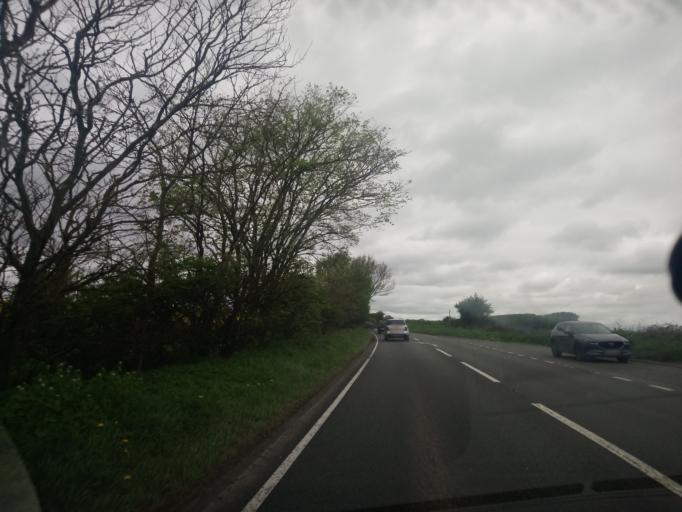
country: GB
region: England
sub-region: Telford and Wrekin
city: Chetwynd
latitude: 52.8170
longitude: -2.4471
